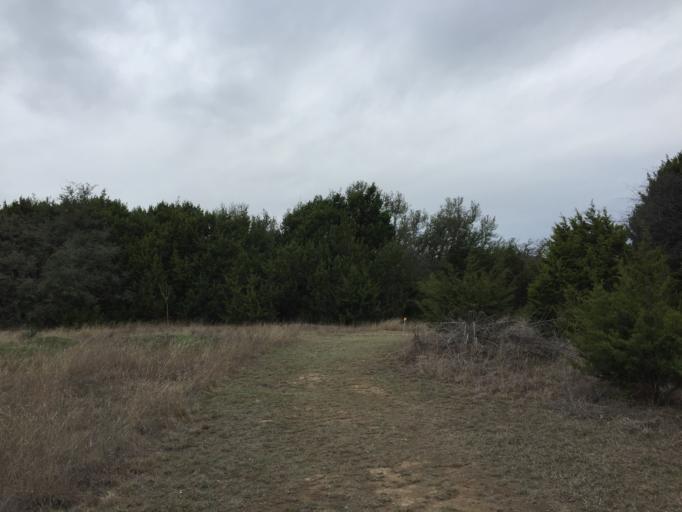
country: US
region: Texas
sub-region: Bell County
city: Fort Hood
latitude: 31.1158
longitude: -97.8137
